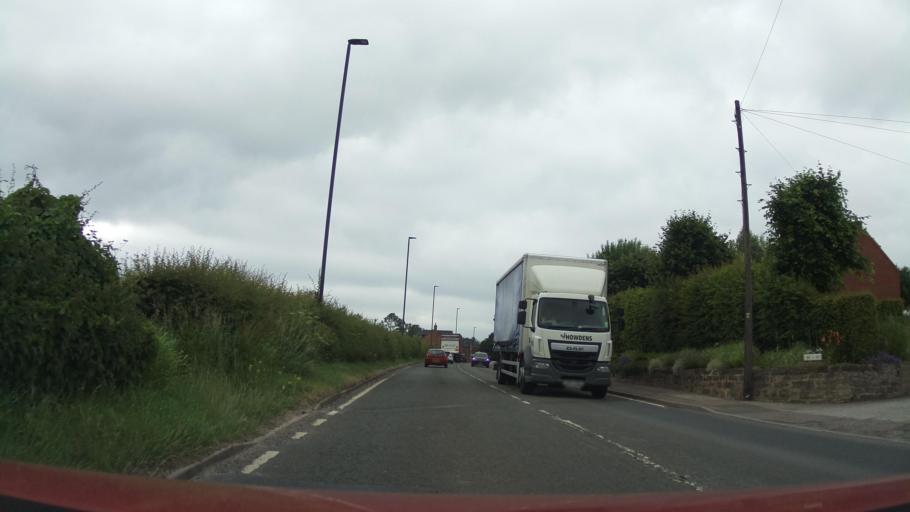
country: GB
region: England
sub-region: Derby
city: Derby
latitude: 52.9337
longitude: -1.5294
